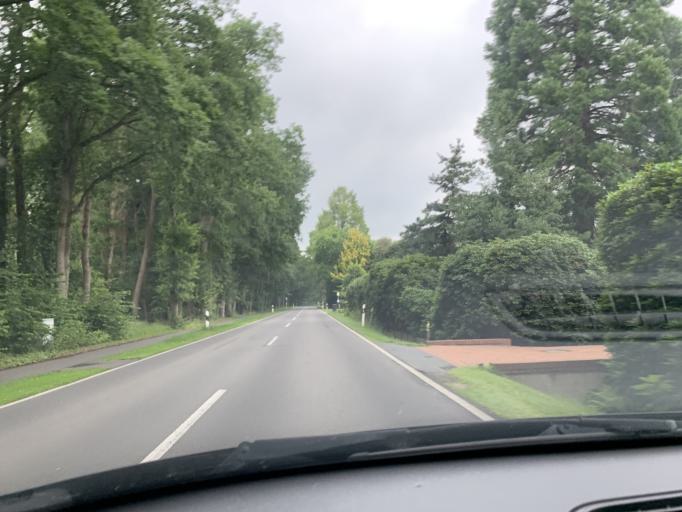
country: DE
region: Lower Saxony
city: Bad Zwischenahn
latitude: 53.2080
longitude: 8.0346
